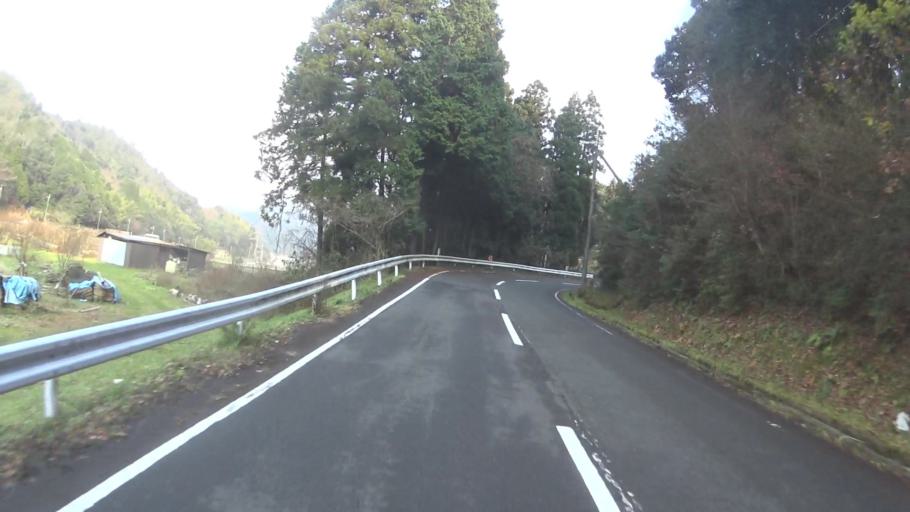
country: JP
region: Kyoto
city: Maizuru
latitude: 35.4448
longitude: 135.3903
